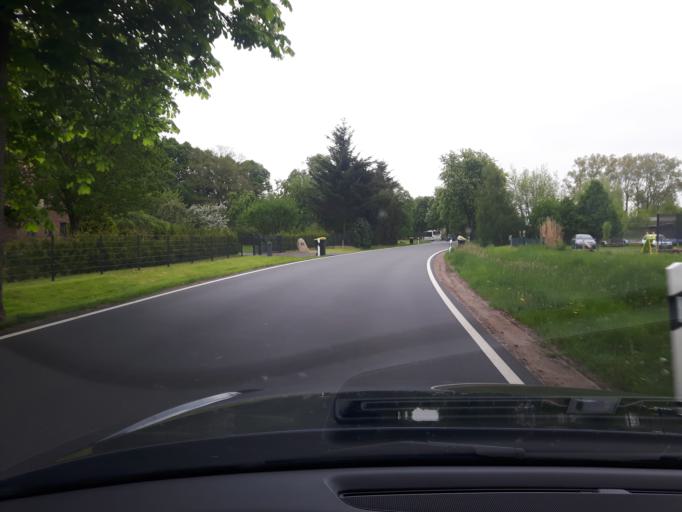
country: DE
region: Mecklenburg-Vorpommern
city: Gnoien
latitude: 54.0268
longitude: 12.6621
